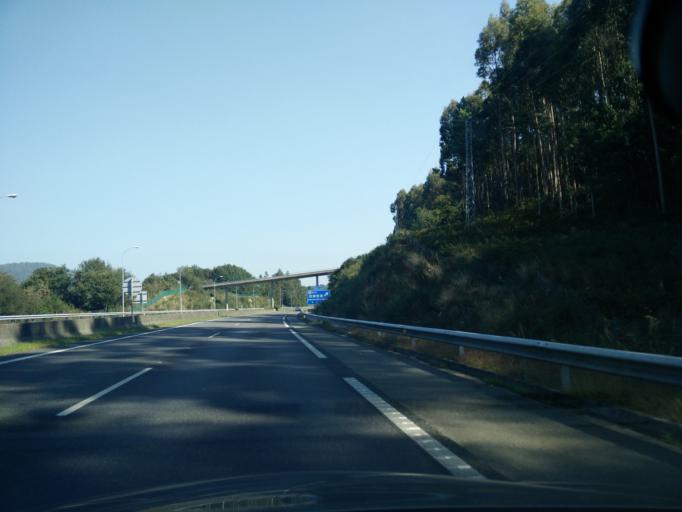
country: ES
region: Galicia
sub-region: Provincia da Coruna
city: Mino
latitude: 43.3690
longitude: -8.1930
